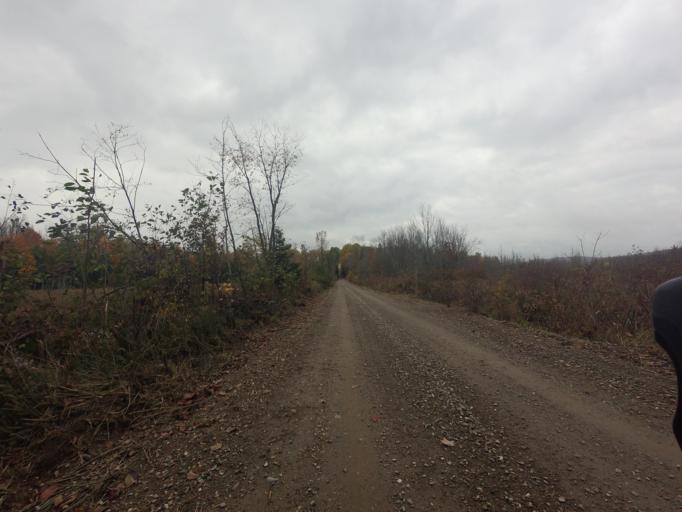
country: CA
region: Ontario
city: Renfrew
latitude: 45.1811
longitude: -76.6842
